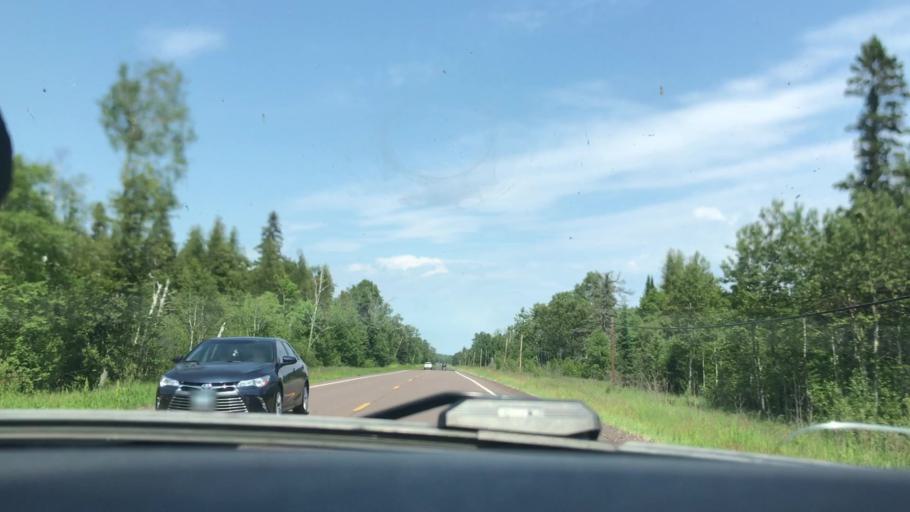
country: US
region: Minnesota
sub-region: Cook County
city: Grand Marais
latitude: 47.6308
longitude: -90.7260
